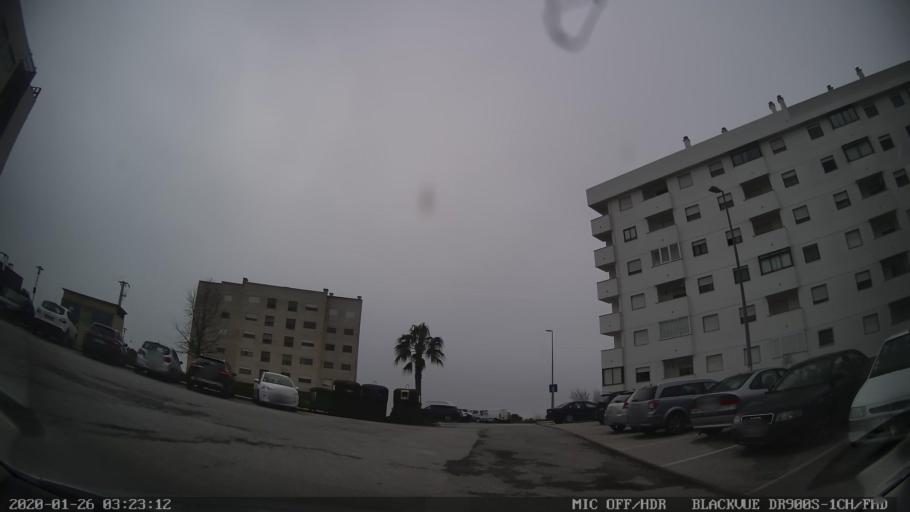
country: PT
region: Santarem
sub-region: Santarem
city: Santarem
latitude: 39.2233
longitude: -8.6923
